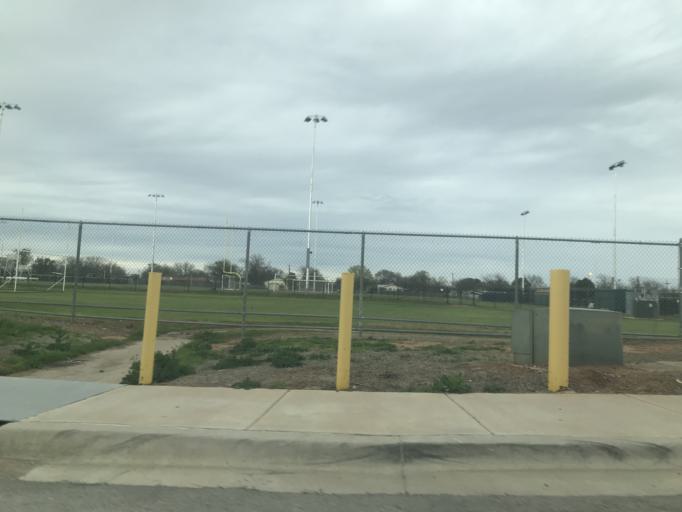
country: US
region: Texas
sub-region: Taylor County
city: Abilene
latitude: 32.4570
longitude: -99.7559
